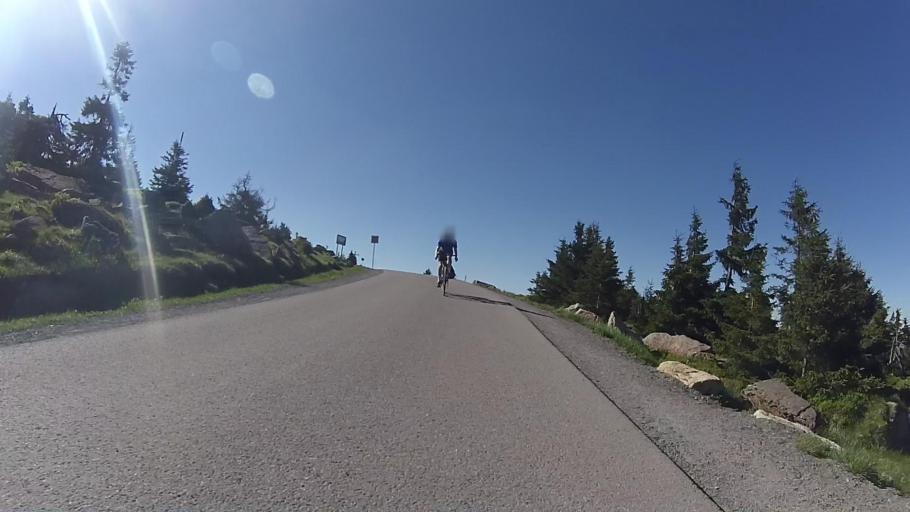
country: DE
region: Lower Saxony
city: Braunlage
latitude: 51.7987
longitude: 10.6209
